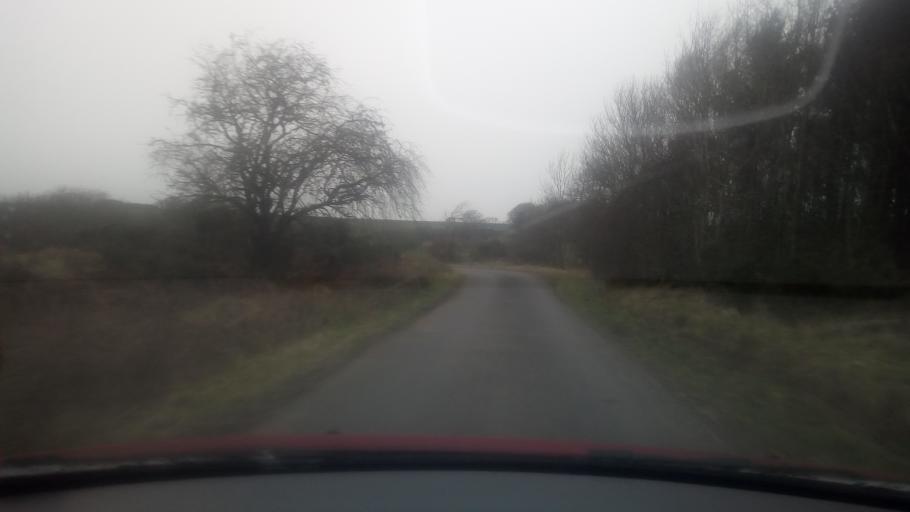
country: GB
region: Scotland
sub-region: The Scottish Borders
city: Hawick
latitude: 55.3828
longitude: -2.6683
